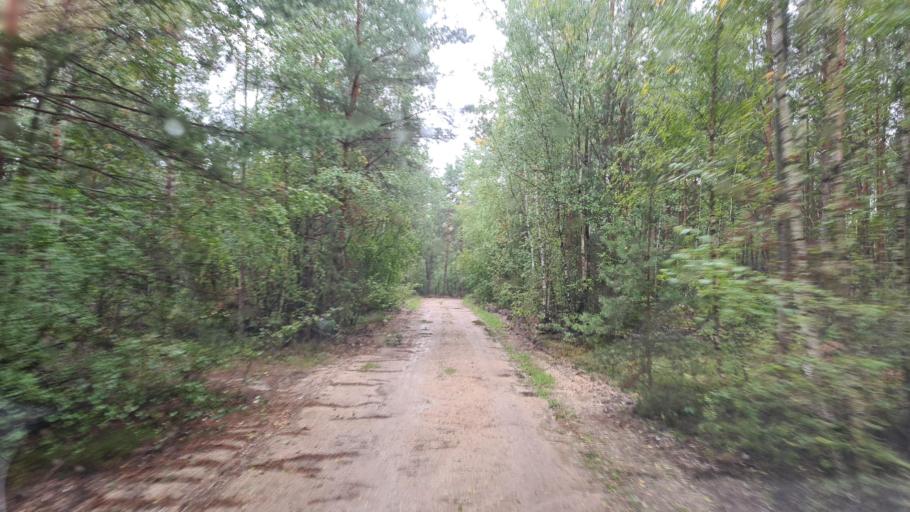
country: DE
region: Brandenburg
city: Sallgast
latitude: 51.5841
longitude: 13.8021
